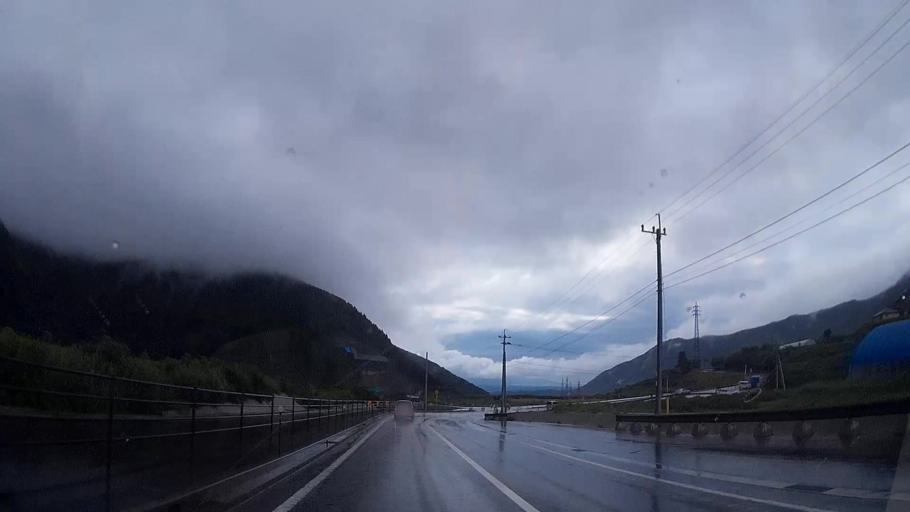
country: JP
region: Kumamoto
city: Ozu
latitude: 32.8757
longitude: 130.9796
